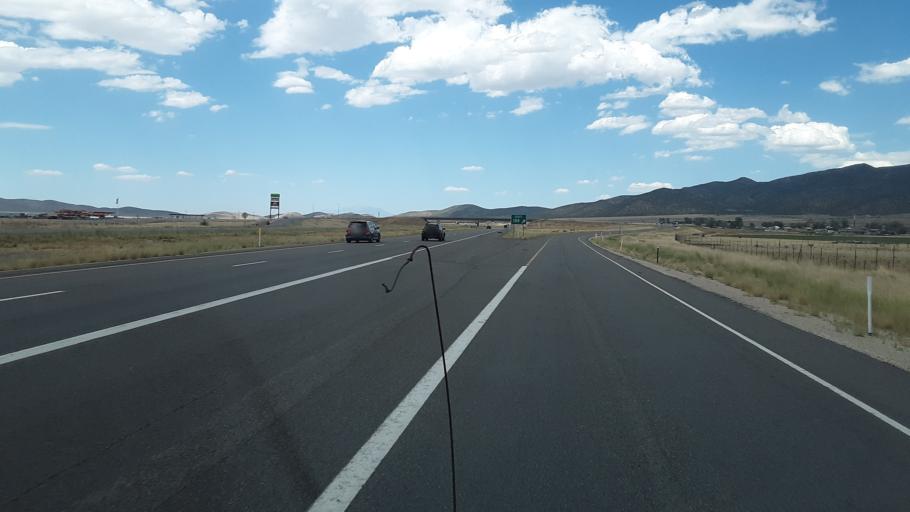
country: US
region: Utah
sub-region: Sanpete County
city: Gunnison
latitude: 39.2483
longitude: -112.1183
